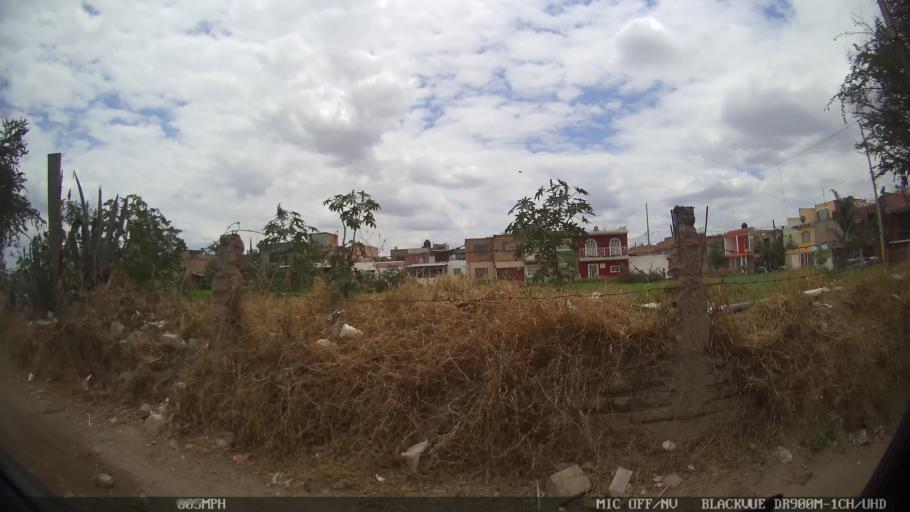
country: MX
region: Jalisco
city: Tlaquepaque
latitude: 20.6463
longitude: -103.2684
